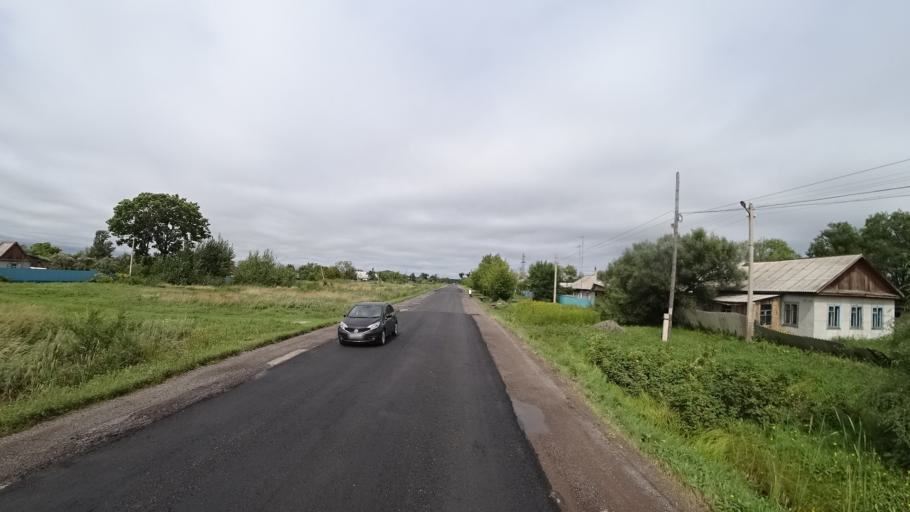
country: RU
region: Primorskiy
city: Monastyrishche
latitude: 44.1978
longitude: 132.4781
